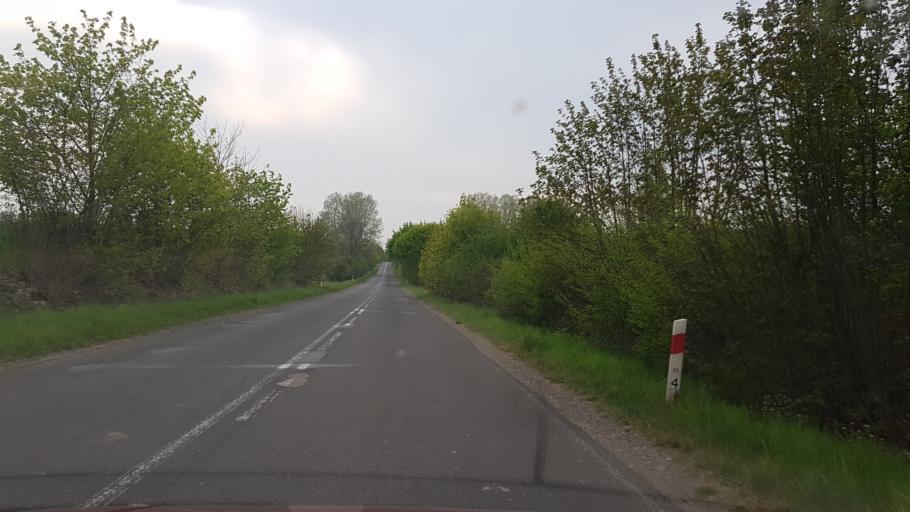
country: PL
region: West Pomeranian Voivodeship
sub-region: Powiat gryfinski
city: Stare Czarnowo
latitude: 53.2882
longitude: 14.7351
